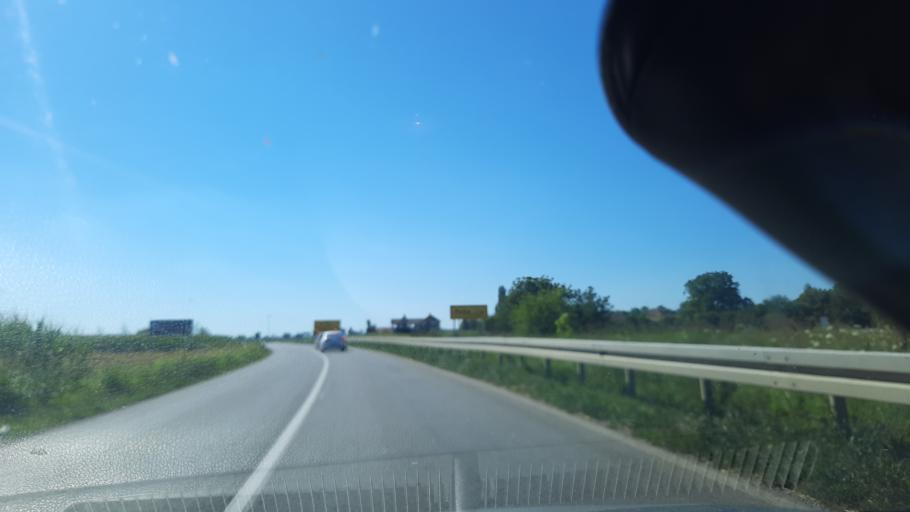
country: RS
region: Autonomna Pokrajina Vojvodina
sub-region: Sremski Okrug
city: Pecinci
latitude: 44.8964
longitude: 19.9705
